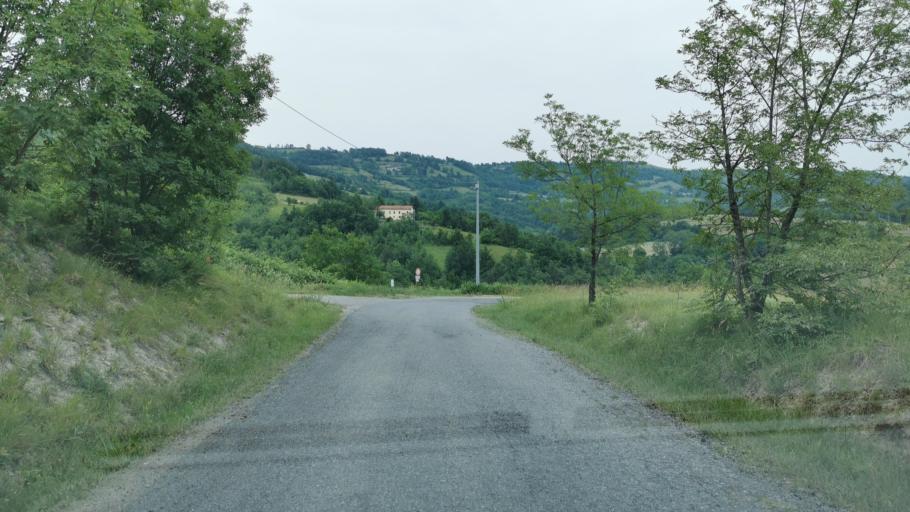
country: IT
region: Piedmont
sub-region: Provincia di Cuneo
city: Paroldo
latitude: 44.4294
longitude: 8.0549
